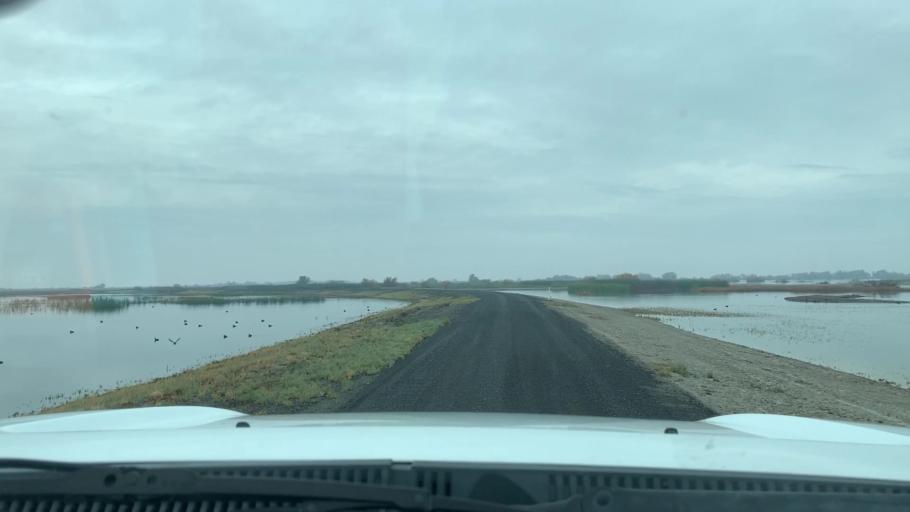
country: US
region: California
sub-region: Kern County
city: Lost Hills
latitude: 35.7415
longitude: -119.6063
